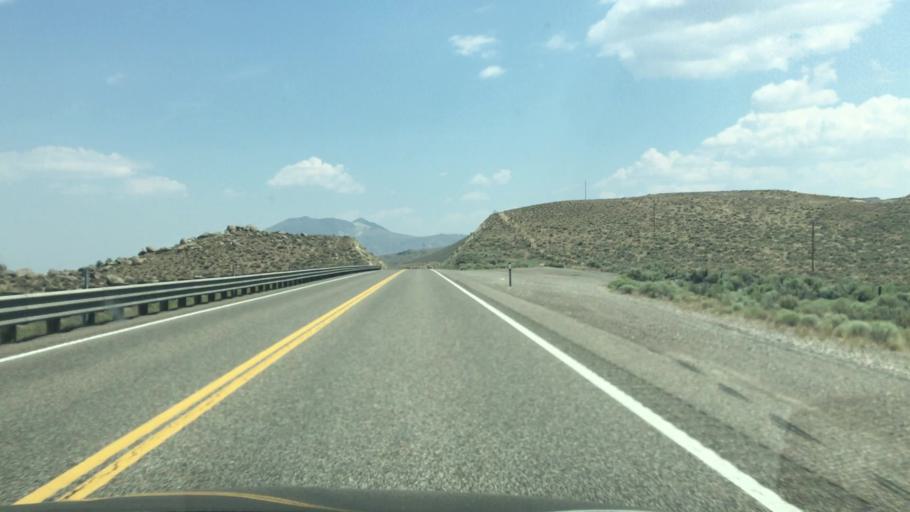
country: US
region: Nevada
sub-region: Elko County
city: Jackpot
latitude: 41.7393
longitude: -114.7818
